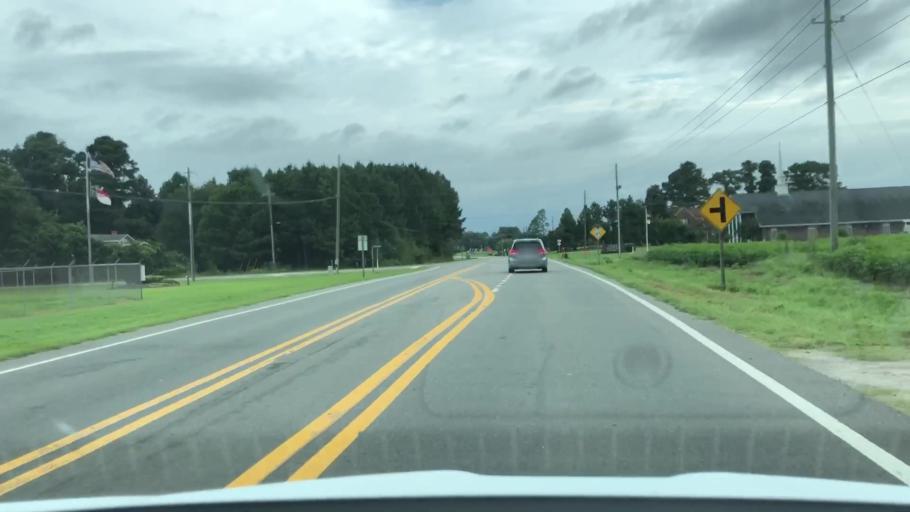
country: US
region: North Carolina
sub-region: Lenoir County
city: Kinston
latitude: 35.2297
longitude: -77.5749
